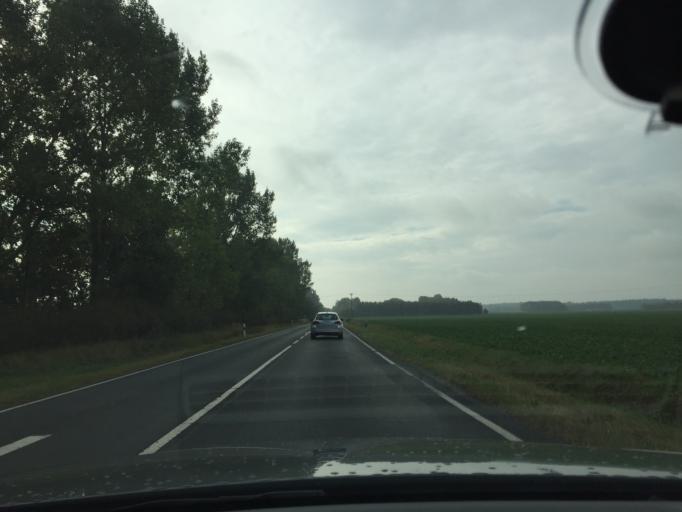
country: DE
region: Mecklenburg-Vorpommern
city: Ostseebad Dierhagen
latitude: 54.2391
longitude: 12.3623
